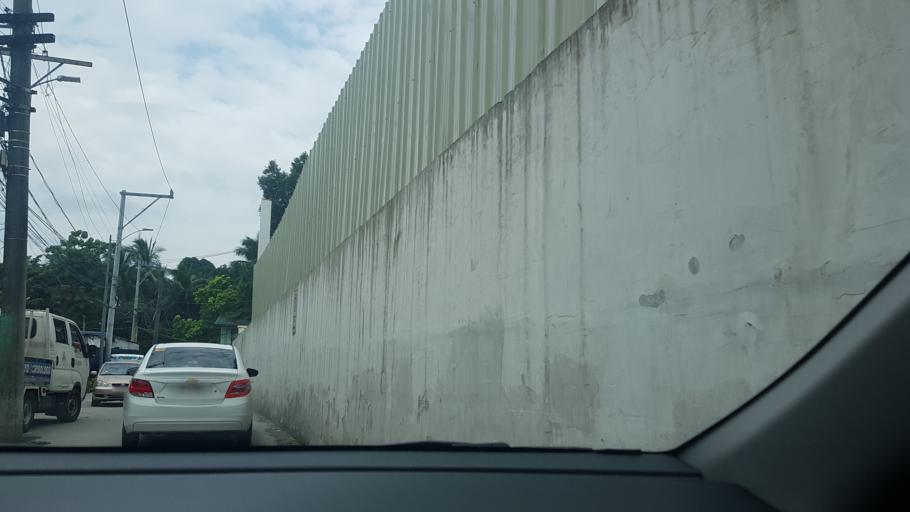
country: PH
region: Calabarzon
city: Del Monte
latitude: 14.6540
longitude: 121.0019
